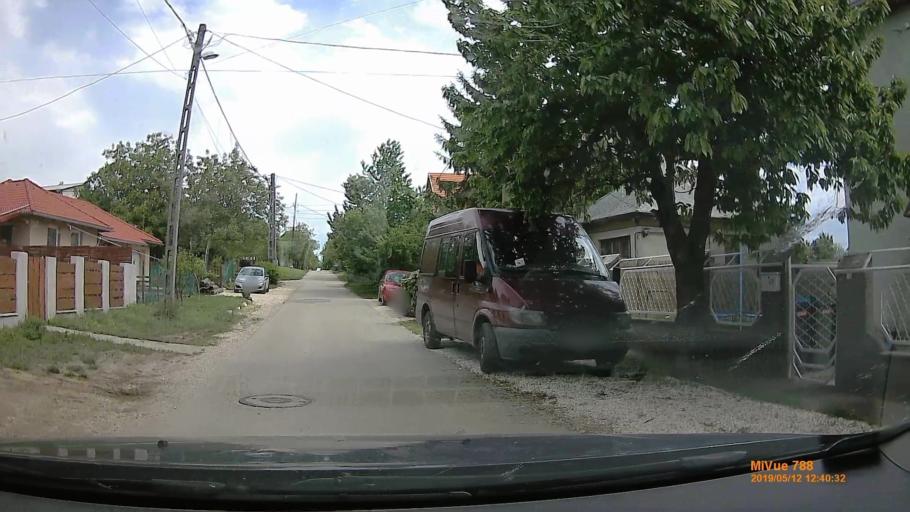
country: HU
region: Pest
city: Ecser
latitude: 47.4580
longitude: 19.3152
